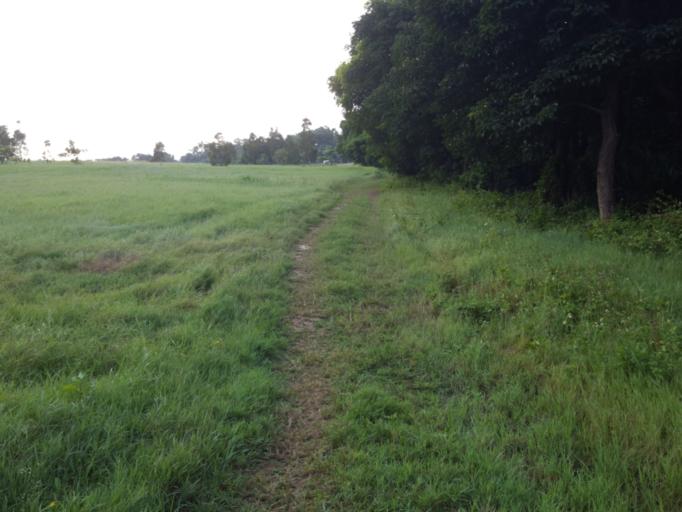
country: TW
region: Taiwan
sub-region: Hsinchu
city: Hsinchu
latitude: 24.7745
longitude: 120.9291
